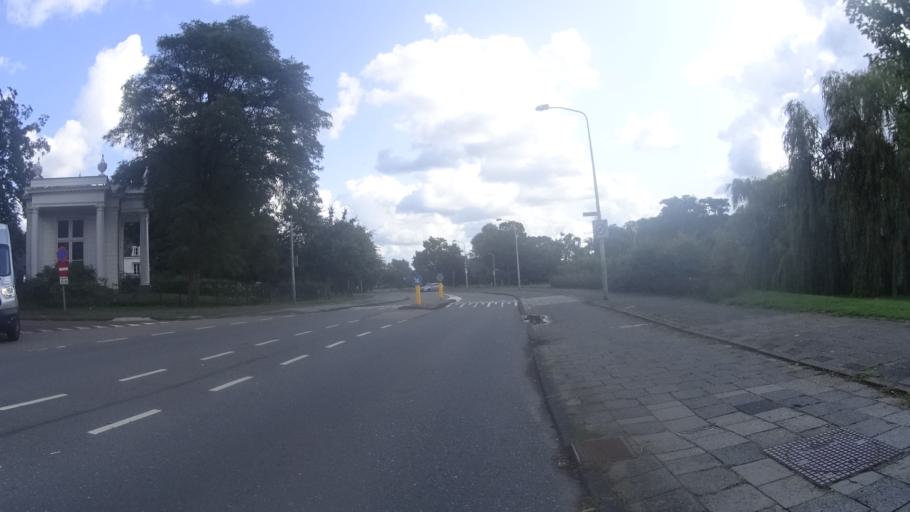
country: NL
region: North Holland
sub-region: Gemeente Bloemendaal
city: Bloemendaal
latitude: 52.4065
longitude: 4.6239
